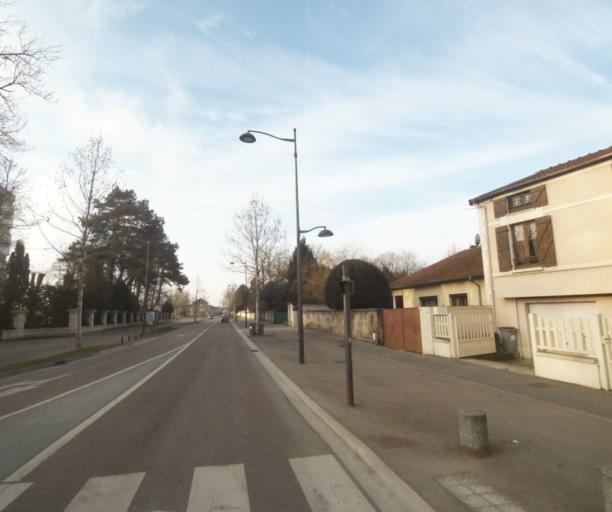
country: FR
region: Champagne-Ardenne
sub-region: Departement de la Haute-Marne
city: Saint-Dizier
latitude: 48.6445
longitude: 4.9530
